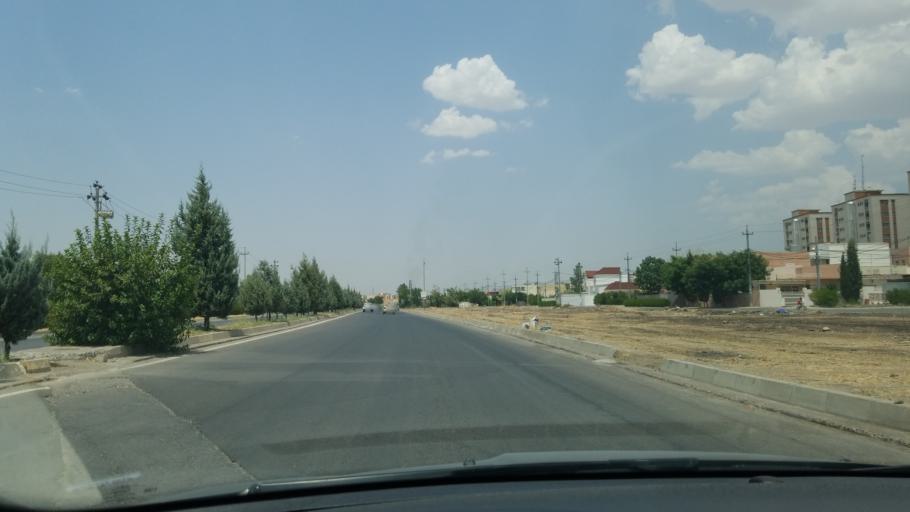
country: IQ
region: Arbil
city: Erbil
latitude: 36.1675
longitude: 44.0587
